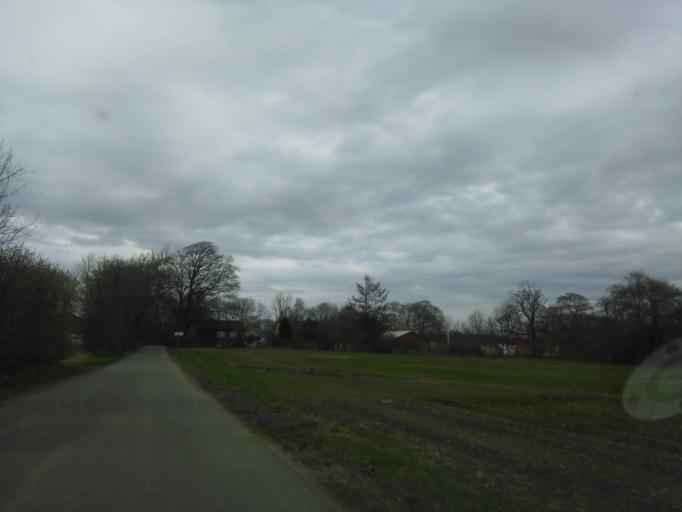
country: DK
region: Central Jutland
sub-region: Skanderborg Kommune
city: Stilling
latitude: 56.0803
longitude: 9.9987
